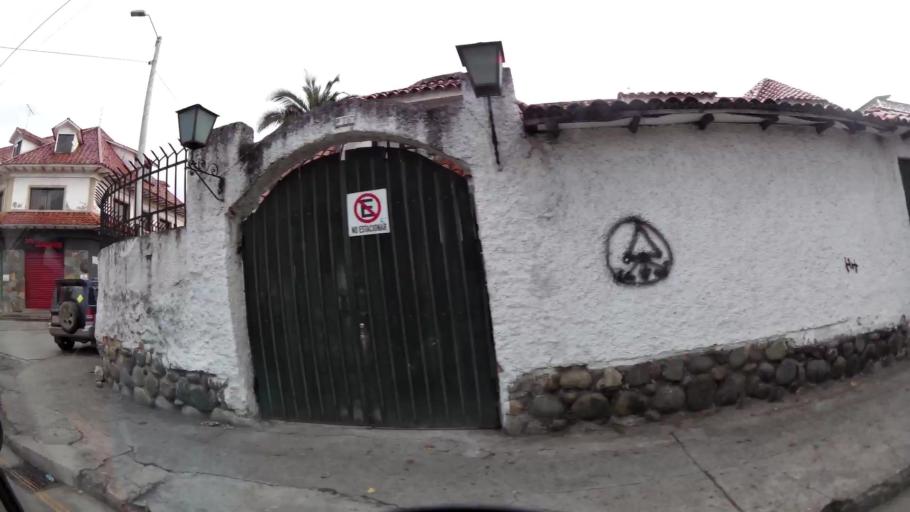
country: EC
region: Azuay
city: Cuenca
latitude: -2.9091
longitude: -79.0042
